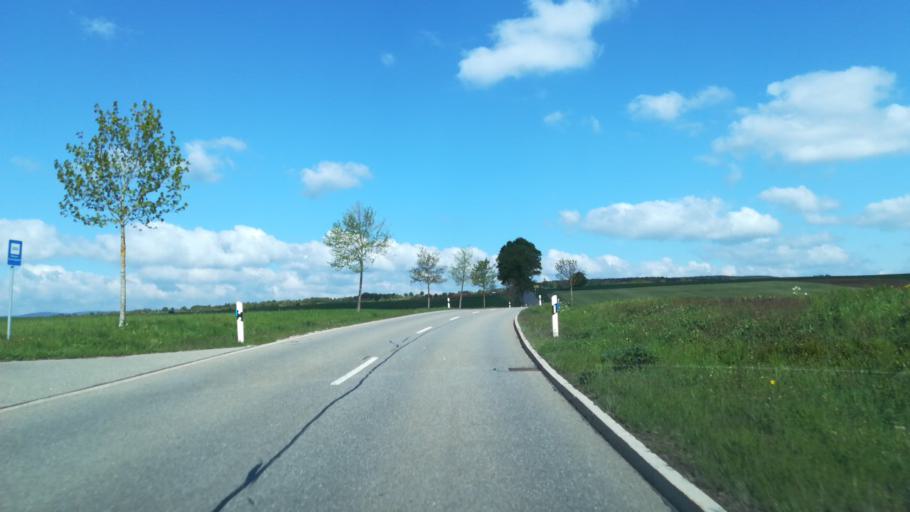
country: DE
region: Baden-Wuerttemberg
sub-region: Freiburg Region
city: Eggingen
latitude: 47.7591
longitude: 8.3831
